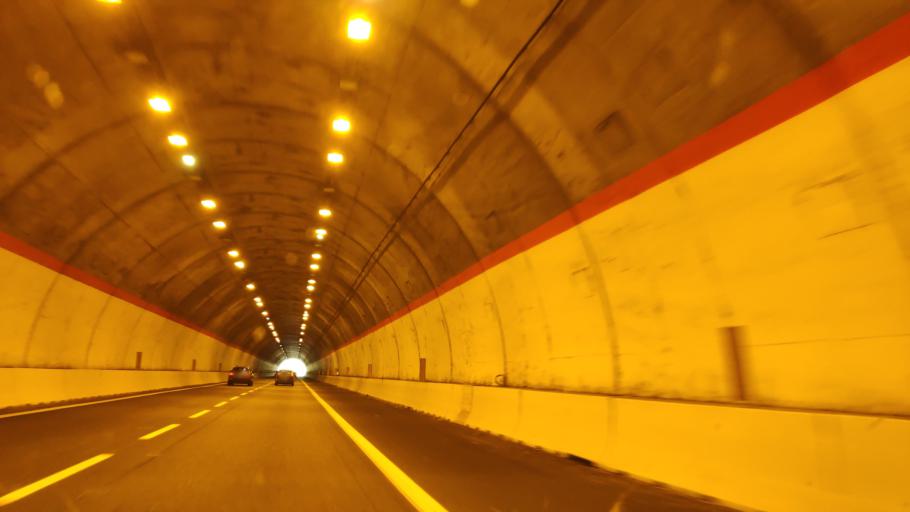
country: IT
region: Campania
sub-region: Provincia di Salerno
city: Auletta
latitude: 40.5343
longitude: 15.4233
